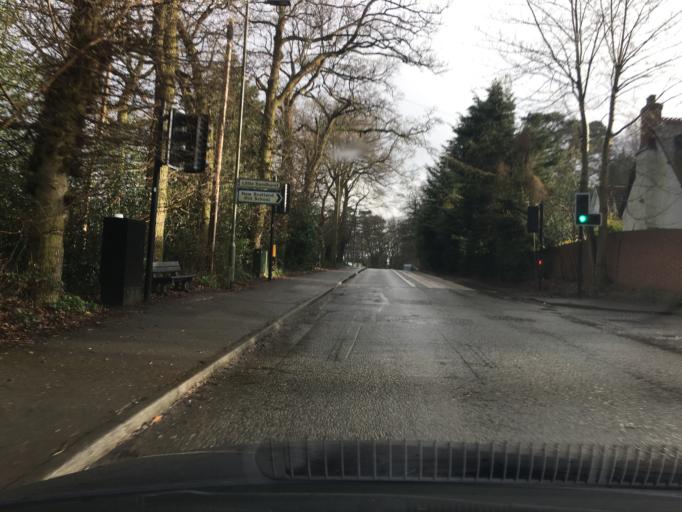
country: GB
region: England
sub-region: Bracknell Forest
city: Sandhurst
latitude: 51.3535
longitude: -0.7989
